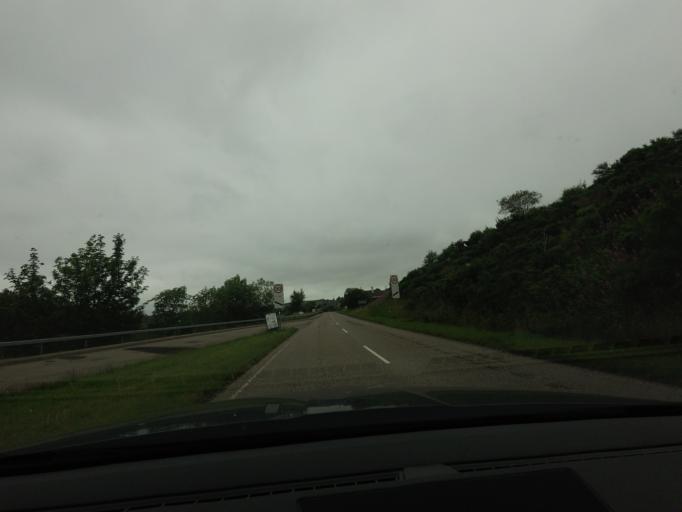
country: GB
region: Scotland
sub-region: Highland
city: Alness
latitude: 58.0180
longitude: -4.4031
